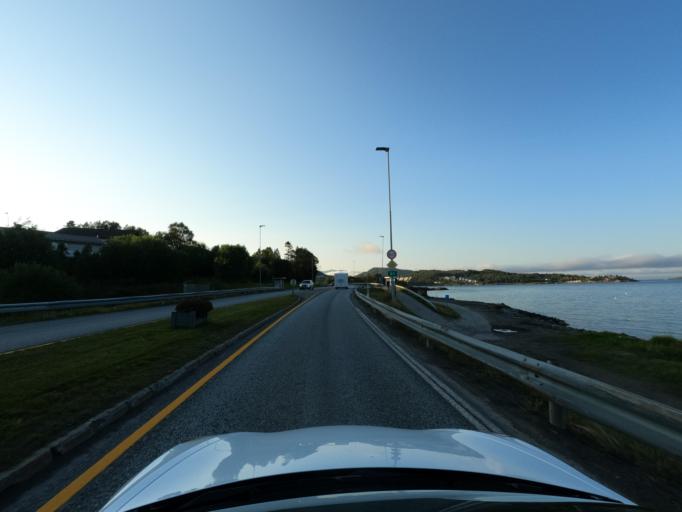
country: NO
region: Troms
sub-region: Harstad
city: Harstad
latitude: 68.7631
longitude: 16.5605
